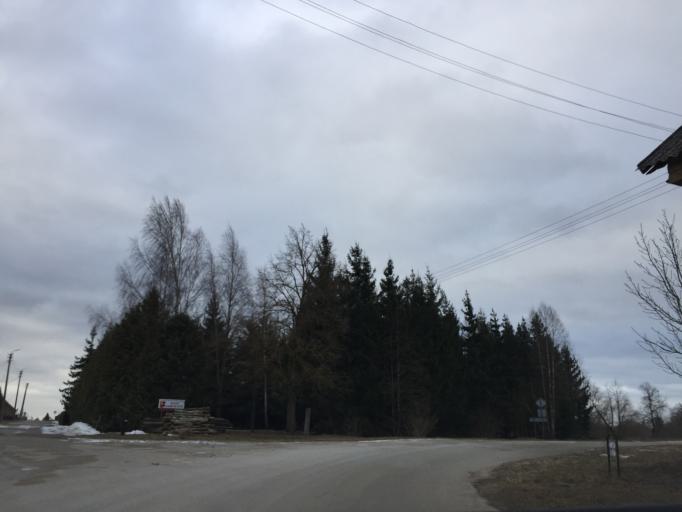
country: LT
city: Zagare
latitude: 56.3557
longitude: 23.2567
